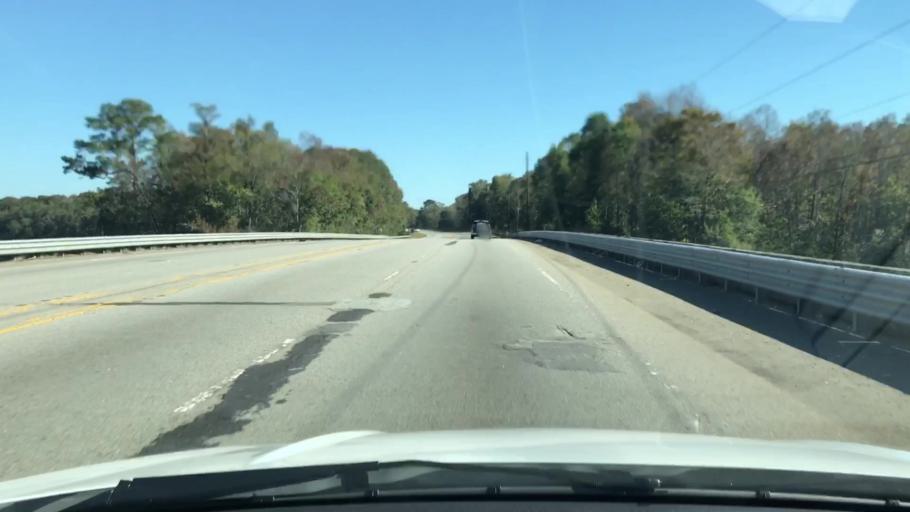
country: US
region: South Carolina
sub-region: Charleston County
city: Ravenel
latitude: 32.7651
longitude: -80.4467
